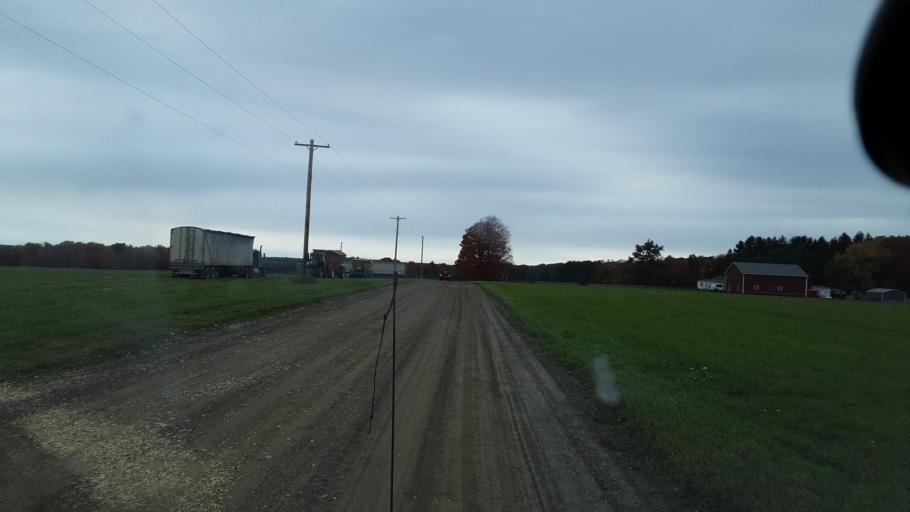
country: US
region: New York
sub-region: Allegany County
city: Andover
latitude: 42.0905
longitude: -77.7958
